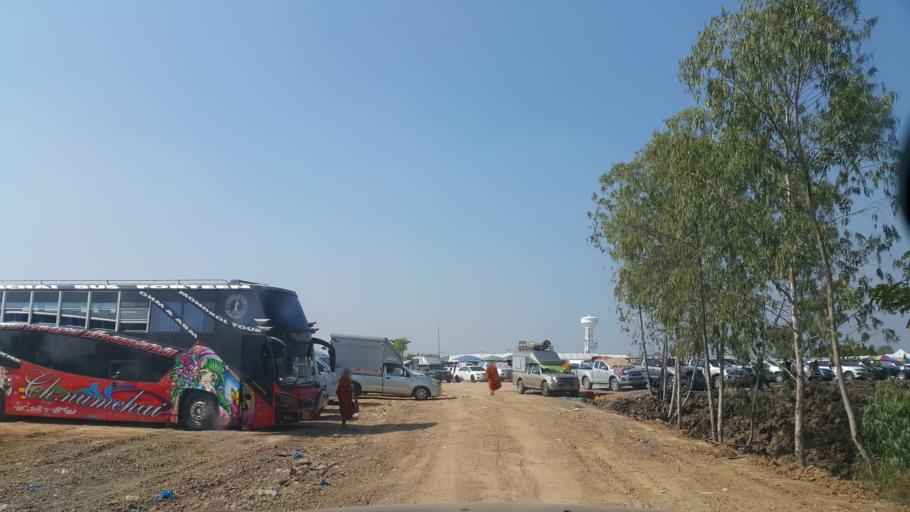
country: TH
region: Khon Kaen
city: Khon Kaen
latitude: 16.5111
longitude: 102.8722
